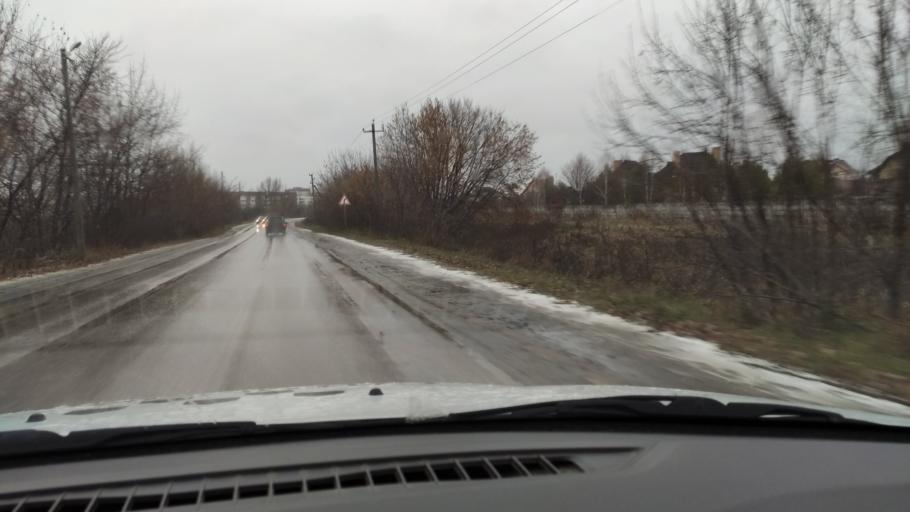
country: RU
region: Perm
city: Kondratovo
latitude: 57.9696
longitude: 56.1152
